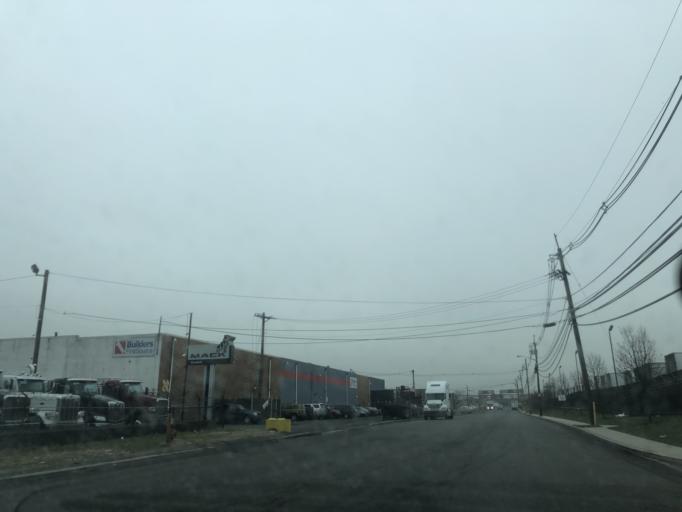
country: US
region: New Jersey
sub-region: Union County
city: Elizabeth
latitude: 40.6665
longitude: -74.1876
